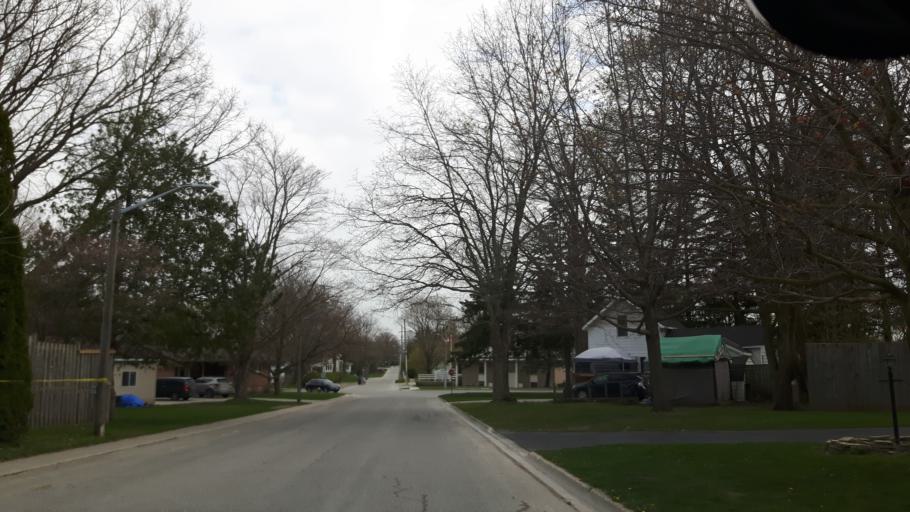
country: CA
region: Ontario
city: Bluewater
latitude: 43.6204
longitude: -81.5452
